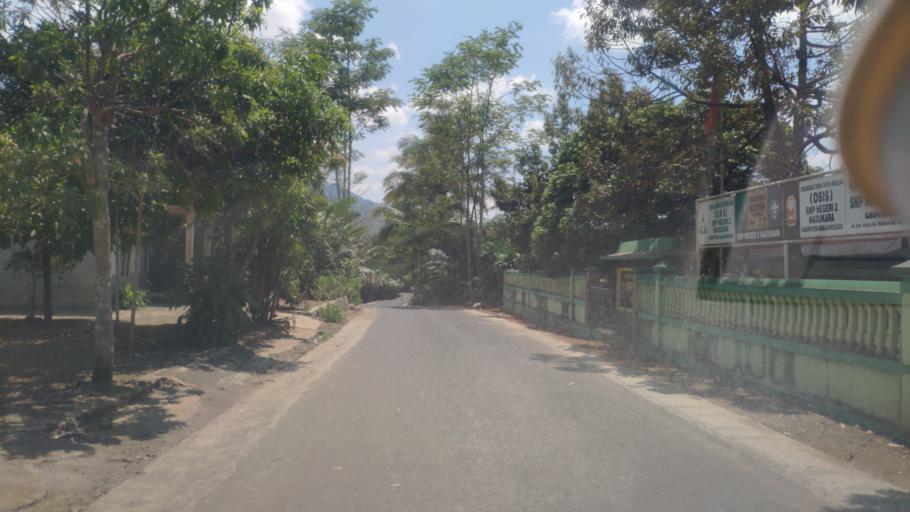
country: ID
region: Central Java
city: Wonosobo
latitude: -7.3568
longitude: 109.7176
